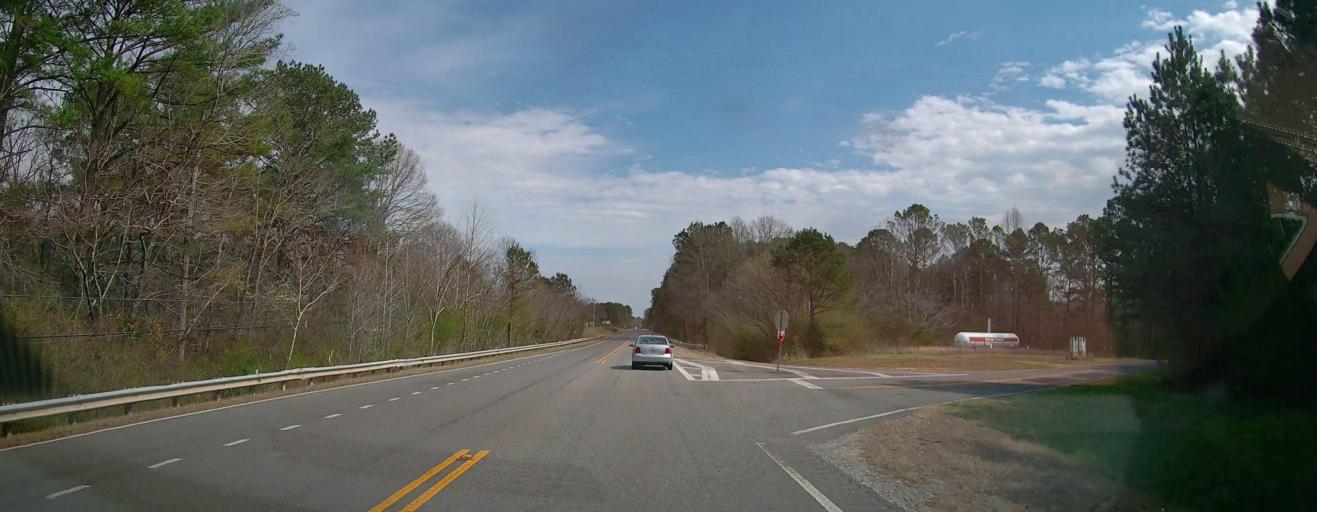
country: US
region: Alabama
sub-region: Walker County
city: Carbon Hill
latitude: 33.9096
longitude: -87.5576
